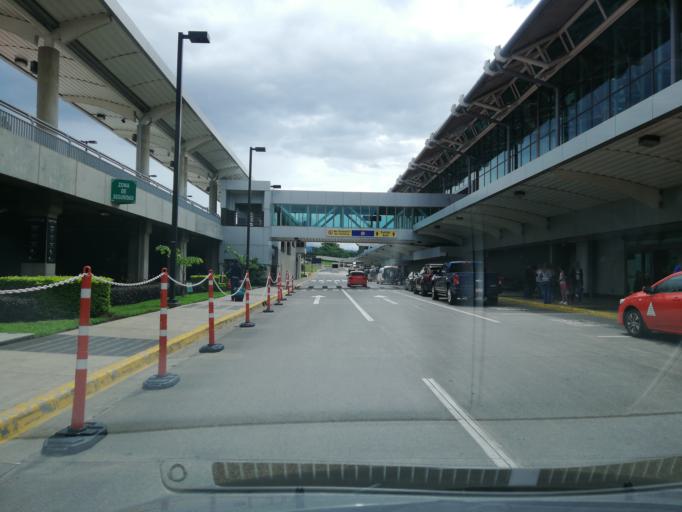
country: CR
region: Alajuela
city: Alajuela
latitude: 9.9980
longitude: -84.2047
